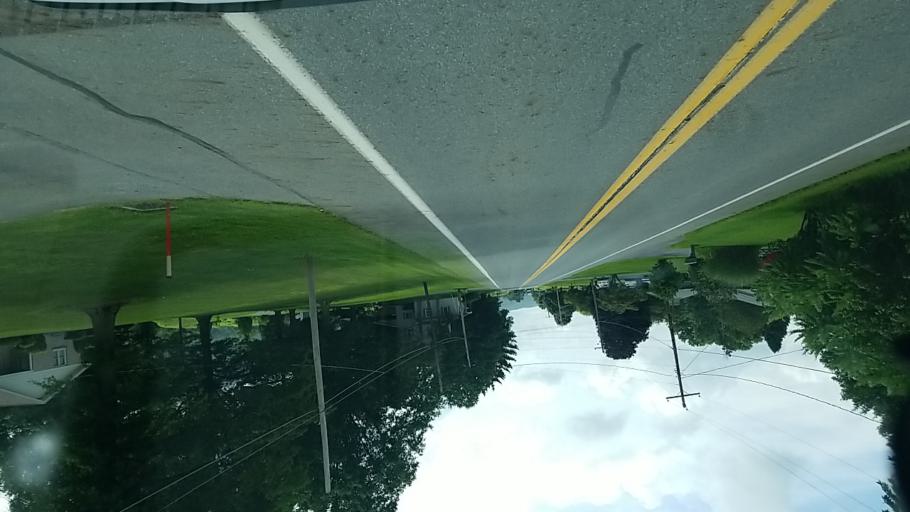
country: US
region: Pennsylvania
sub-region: Dauphin County
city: Elizabethville
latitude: 40.5454
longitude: -76.8543
